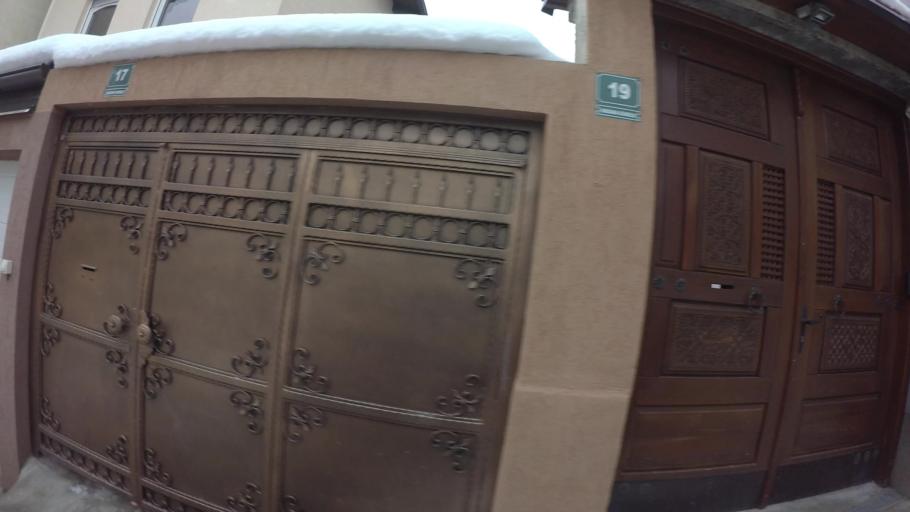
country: BA
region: Federation of Bosnia and Herzegovina
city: Kobilja Glava
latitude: 43.8641
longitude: 18.4318
